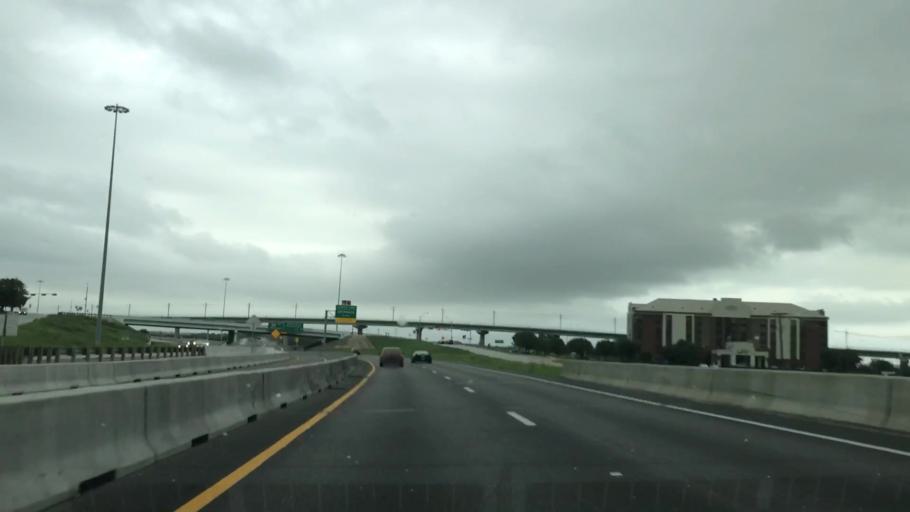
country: US
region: Texas
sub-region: Dallas County
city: Irving
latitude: 32.8769
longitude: -96.9462
